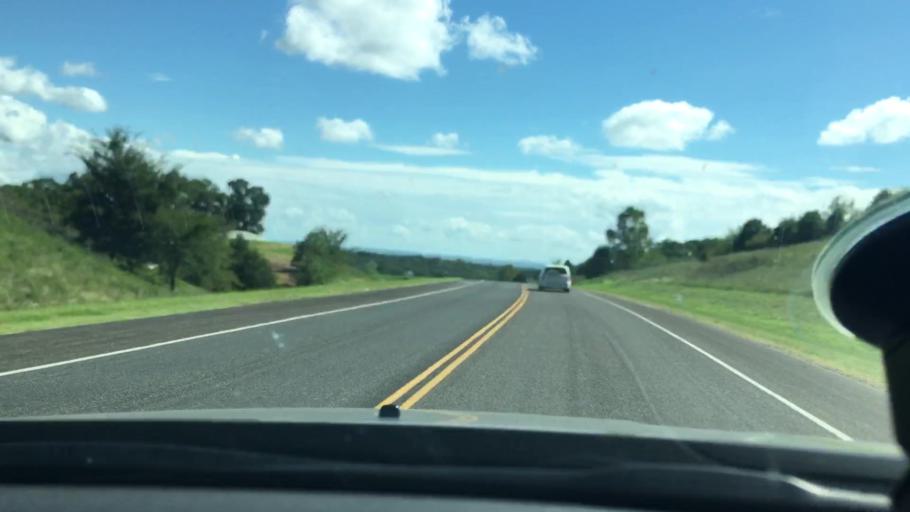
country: US
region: Oklahoma
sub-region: Sequoyah County
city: Vian
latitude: 35.5253
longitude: -94.9745
